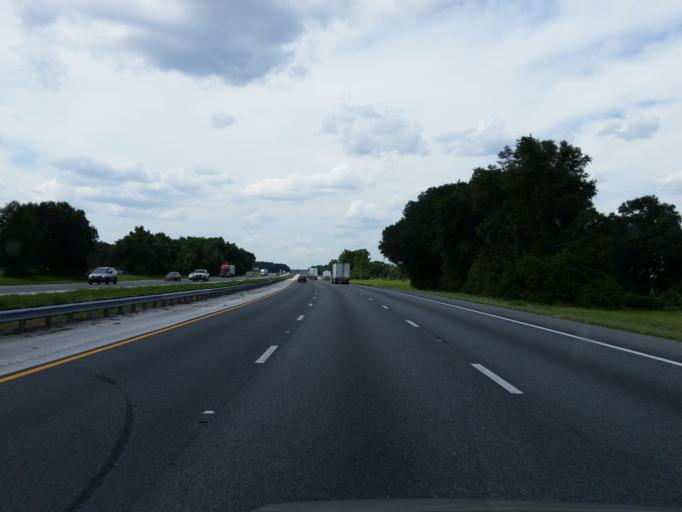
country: US
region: Florida
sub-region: Sumter County
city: Wildwood
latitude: 28.9364
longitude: -82.1121
